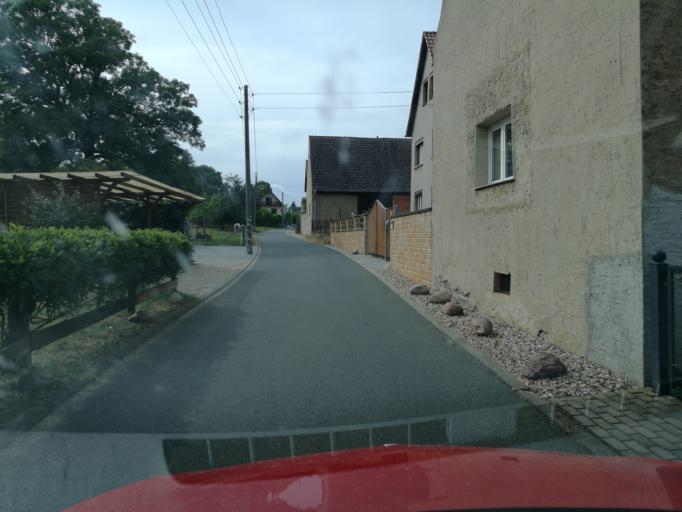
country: DE
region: Saxony
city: Oschatz
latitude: 51.2820
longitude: 13.0796
